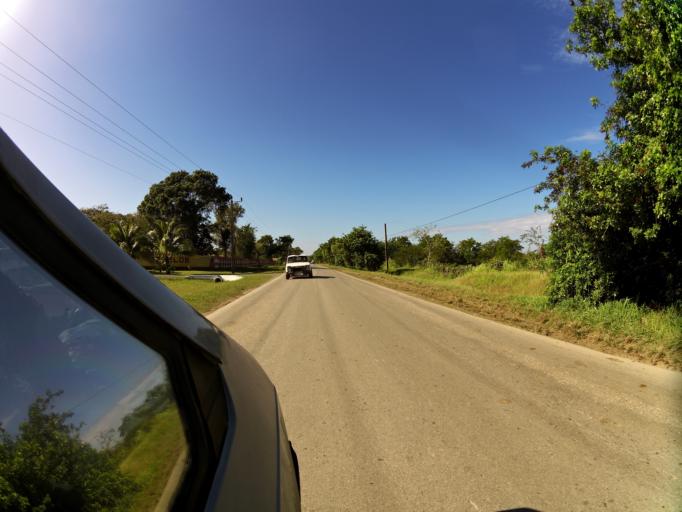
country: CU
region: Las Tunas
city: Las Tunas
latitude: 20.9733
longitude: -76.9095
